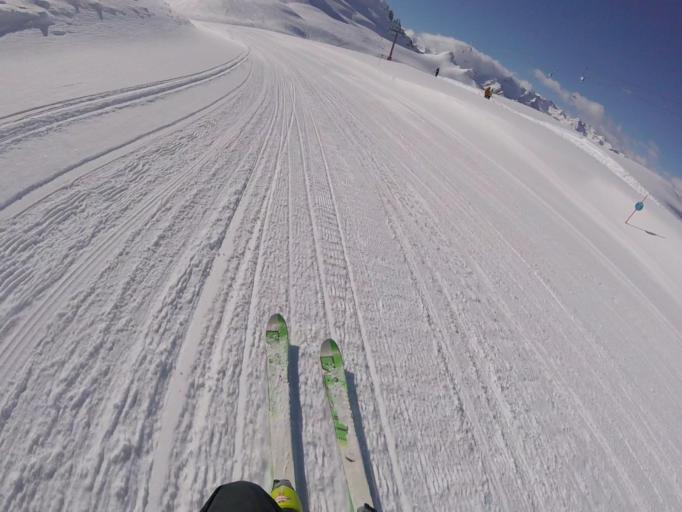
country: ES
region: Catalonia
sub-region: Provincia de Lleida
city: Vielha
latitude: 42.7269
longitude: 0.9393
